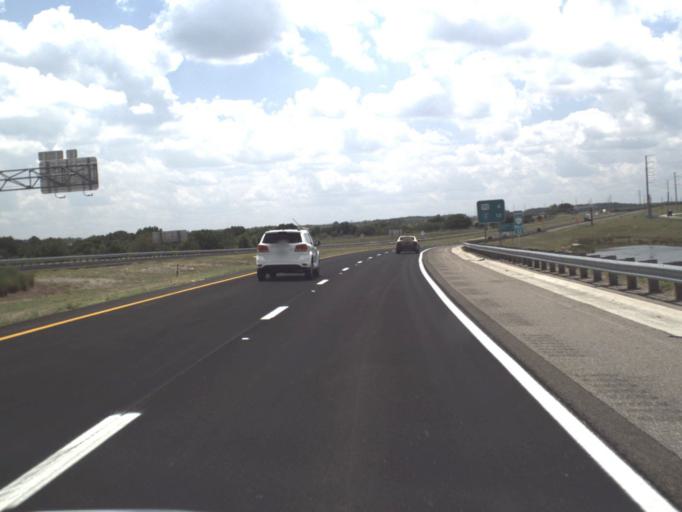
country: US
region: Florida
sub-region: Polk County
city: Citrus Ridge
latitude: 28.4355
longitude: -81.6371
